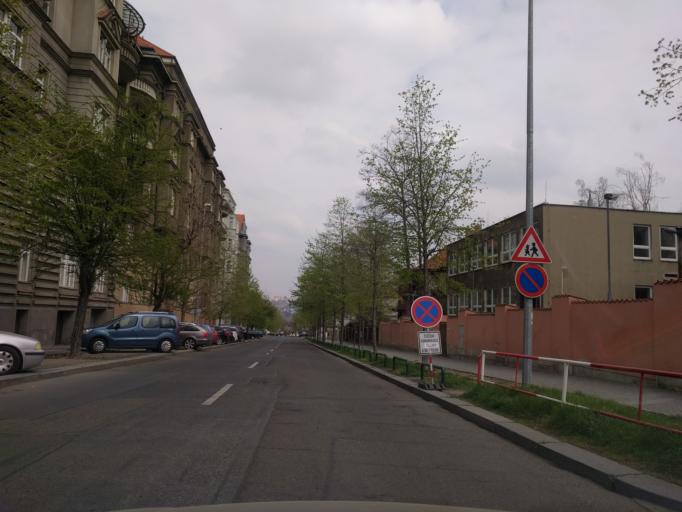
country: CZ
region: Praha
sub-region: Praha 1
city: Mala Strana
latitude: 50.1022
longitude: 14.4051
